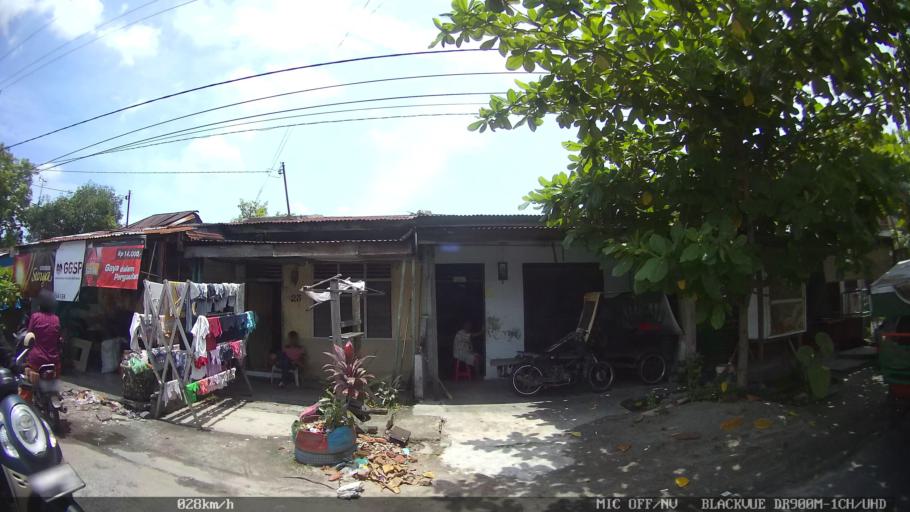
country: ID
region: North Sumatra
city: Percut
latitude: 3.5550
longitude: 98.8758
